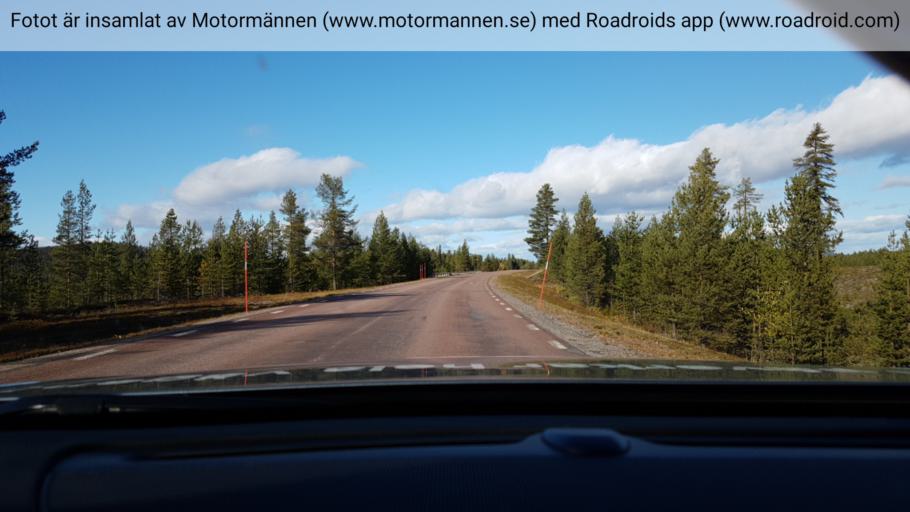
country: SE
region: Norrbotten
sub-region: Arjeplogs Kommun
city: Arjeplog
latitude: 66.0359
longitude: 18.0497
